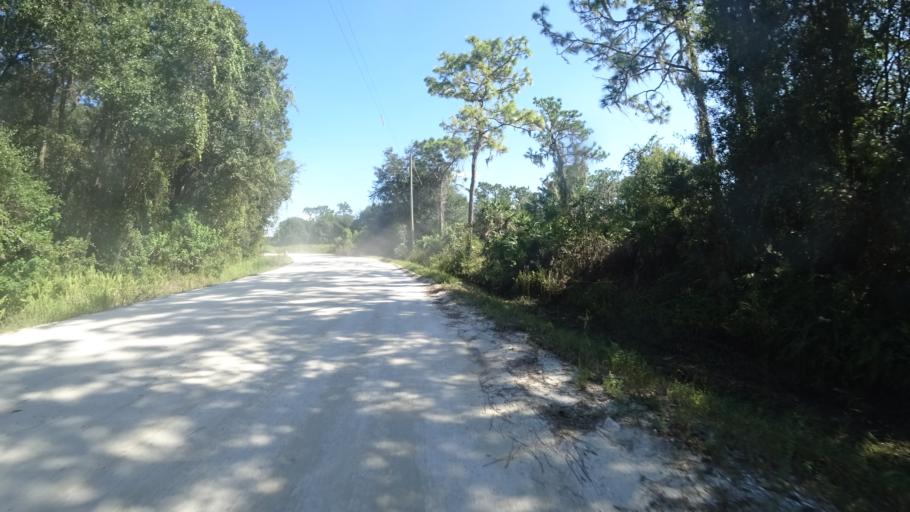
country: US
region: Florida
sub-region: Sarasota County
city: The Meadows
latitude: 27.4523
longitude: -82.3028
